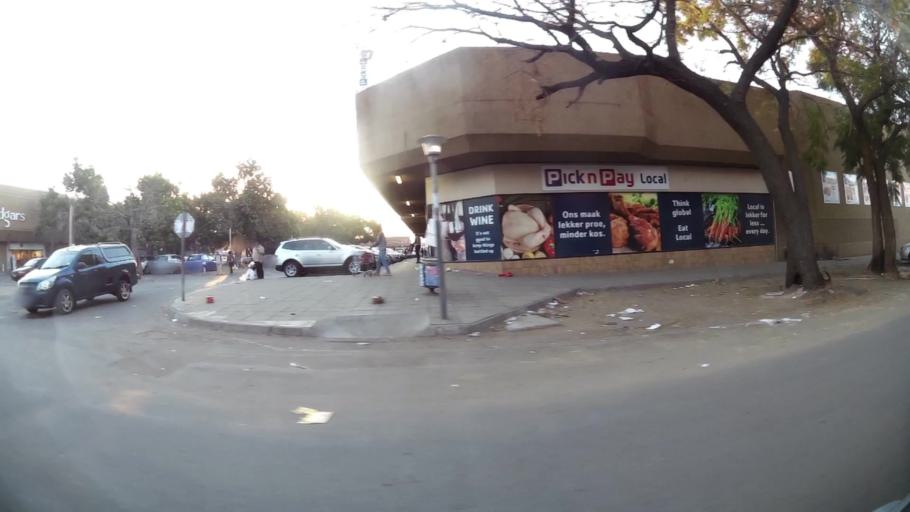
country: ZA
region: North-West
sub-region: Bojanala Platinum District Municipality
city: Rustenburg
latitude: -25.6677
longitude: 27.2430
